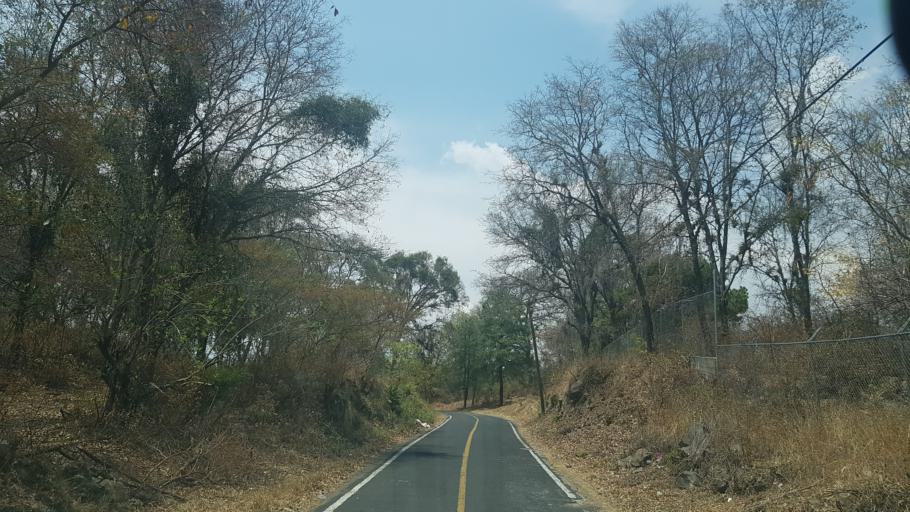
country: MX
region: Puebla
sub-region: Tochimilco
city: La Magdalena Yancuitlalpan
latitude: 18.8849
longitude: -98.5895
